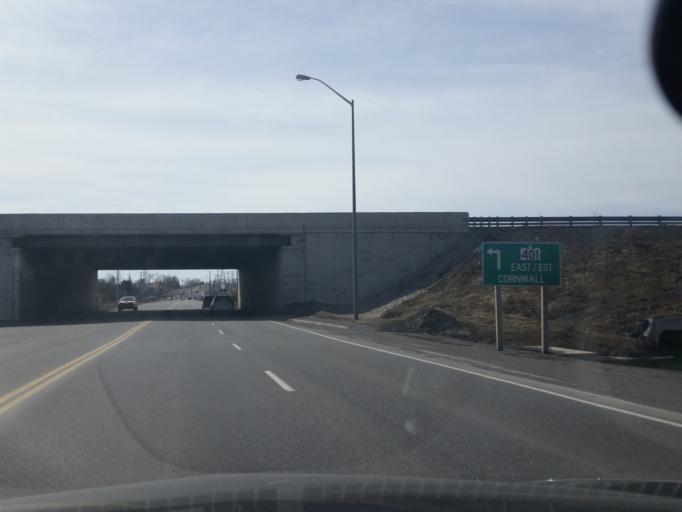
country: CA
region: Ontario
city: Kingston
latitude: 44.2698
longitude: -76.4992
